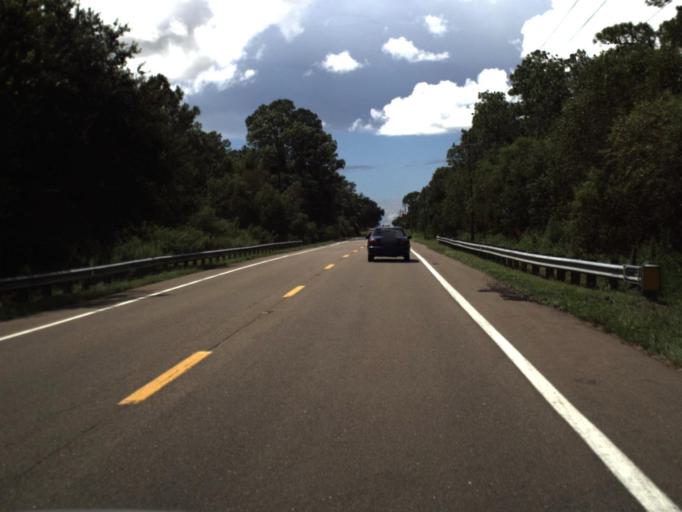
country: US
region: Florida
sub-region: Polk County
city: Frostproof
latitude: 27.7335
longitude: -81.6342
